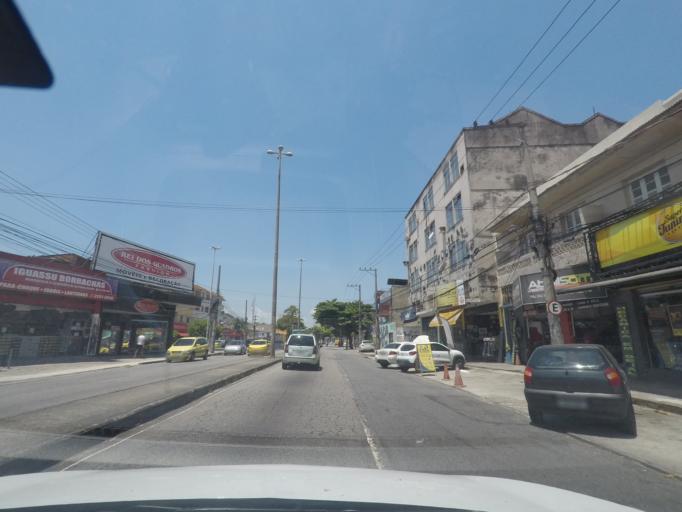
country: BR
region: Rio de Janeiro
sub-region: Rio De Janeiro
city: Rio de Janeiro
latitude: -22.8839
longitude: -43.2971
